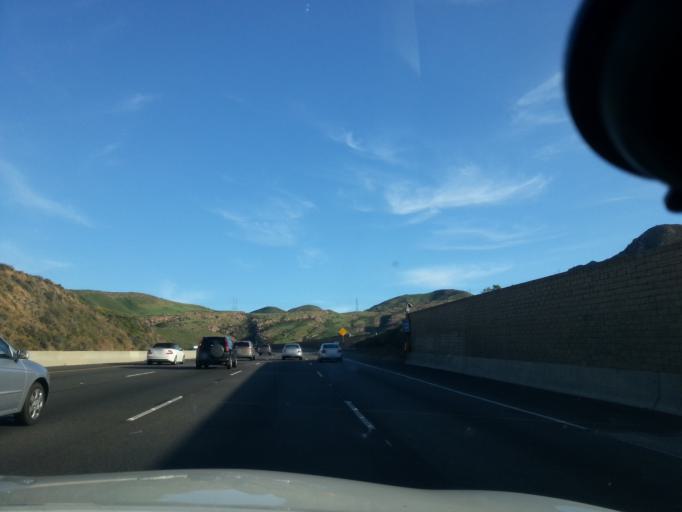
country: US
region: California
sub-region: Ventura County
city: Casa Conejo
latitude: 34.2037
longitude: -118.9810
